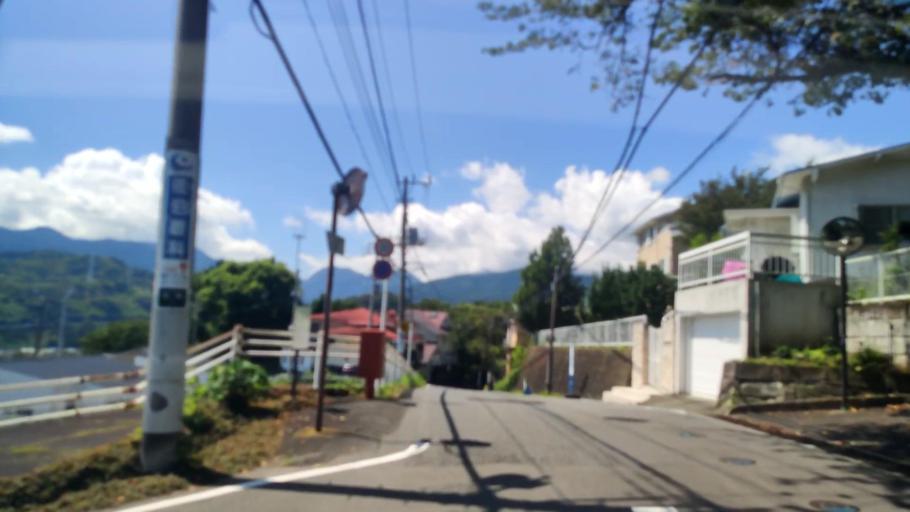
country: JP
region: Kanagawa
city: Odawara
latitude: 35.2515
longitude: 139.1447
